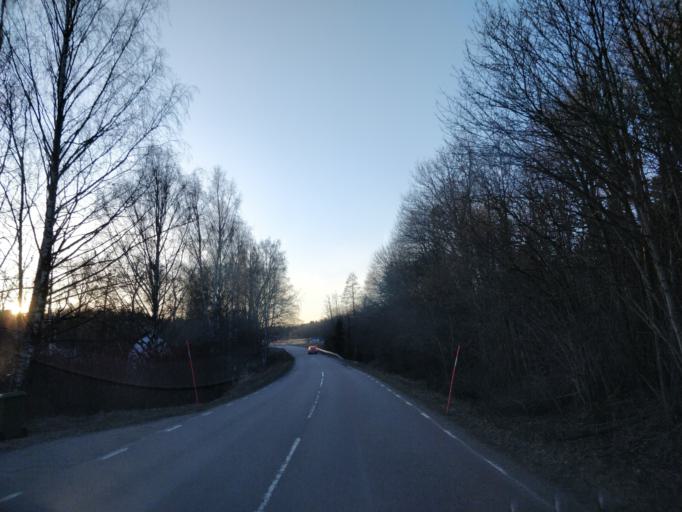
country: SE
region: Uppsala
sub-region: Enkopings Kommun
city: Orsundsbro
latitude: 59.7451
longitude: 17.2768
